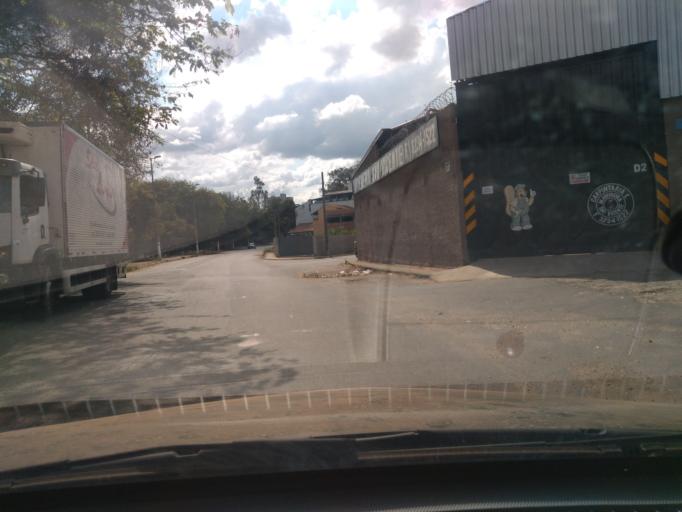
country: BR
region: Minas Gerais
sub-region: Tres Coracoes
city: Tres Coracoes
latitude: -21.7045
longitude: -45.2535
